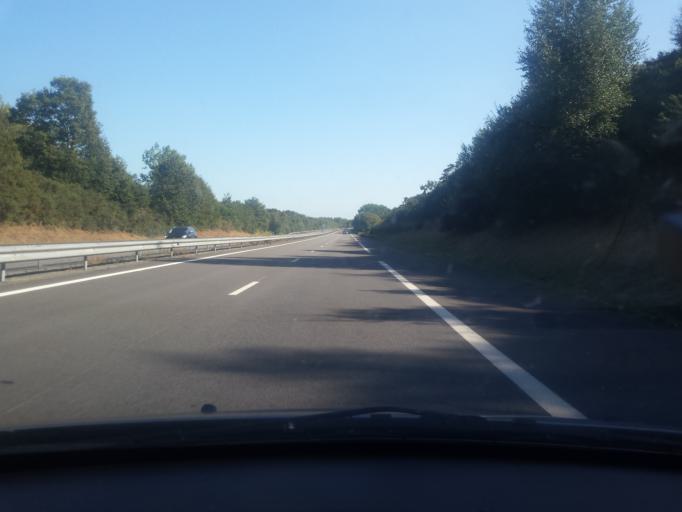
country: FR
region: Brittany
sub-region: Departement du Morbihan
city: Naizin
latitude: 47.9912
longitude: -2.8797
